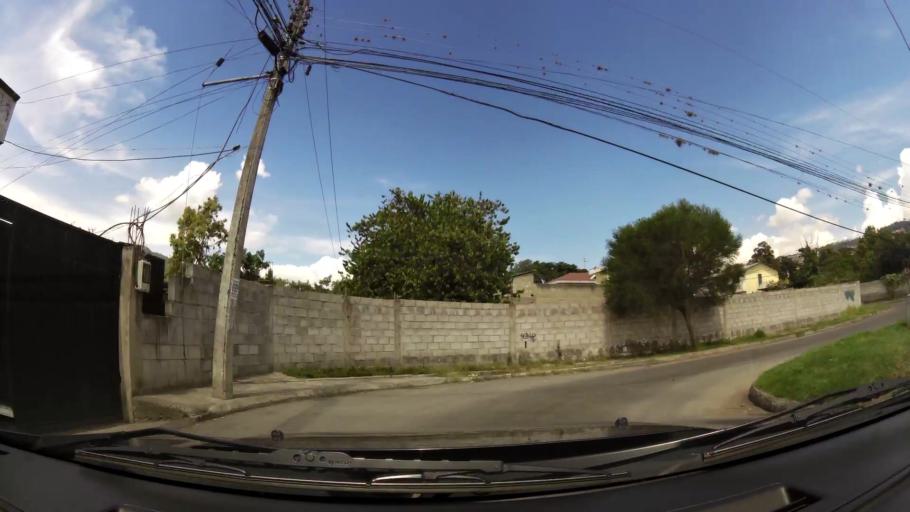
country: EC
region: Pichincha
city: Quito
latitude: -0.2170
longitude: -78.4313
